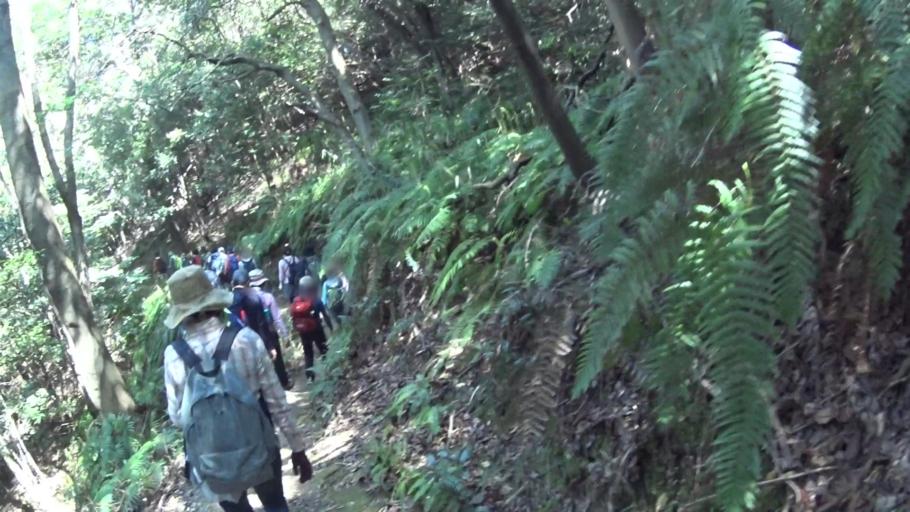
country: JP
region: Kyoto
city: Kyoto
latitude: 34.9850
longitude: 135.7862
